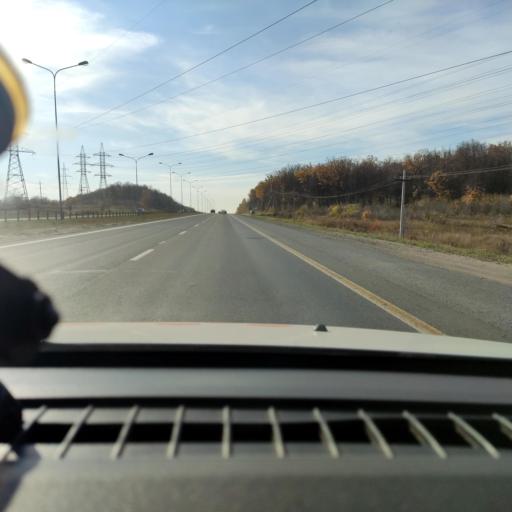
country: RU
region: Samara
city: Novosemeykino
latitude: 53.3709
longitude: 50.3098
